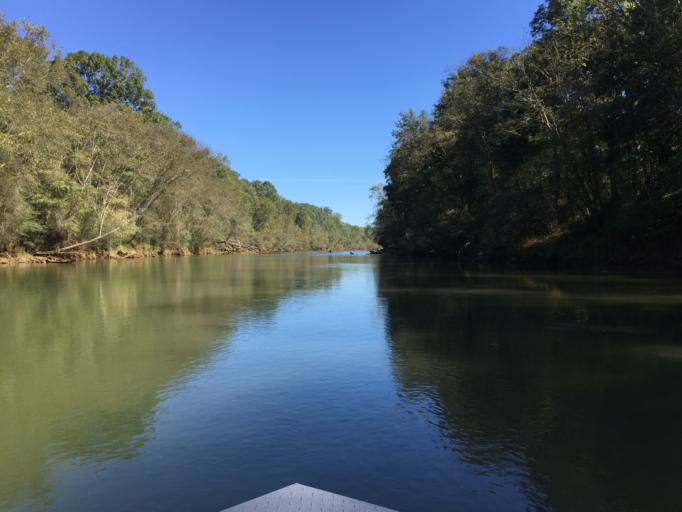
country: US
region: Georgia
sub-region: Gwinnett County
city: Suwanee
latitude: 34.0408
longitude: -84.1133
